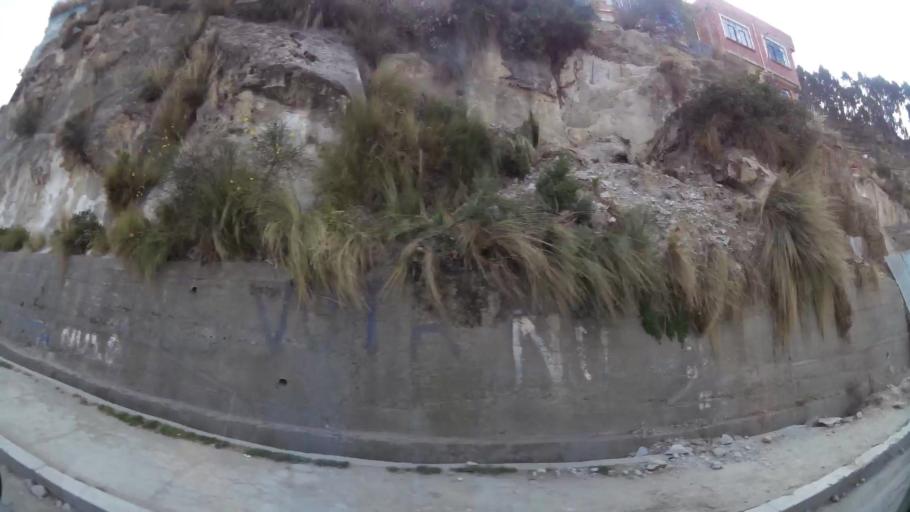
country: BO
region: La Paz
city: La Paz
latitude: -16.4689
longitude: -68.1202
